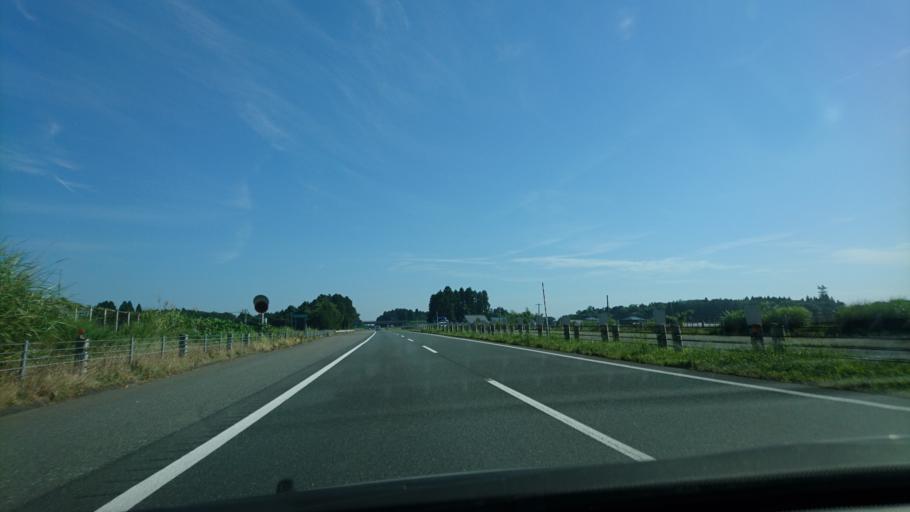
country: JP
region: Iwate
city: Mizusawa
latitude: 39.0961
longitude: 141.1137
